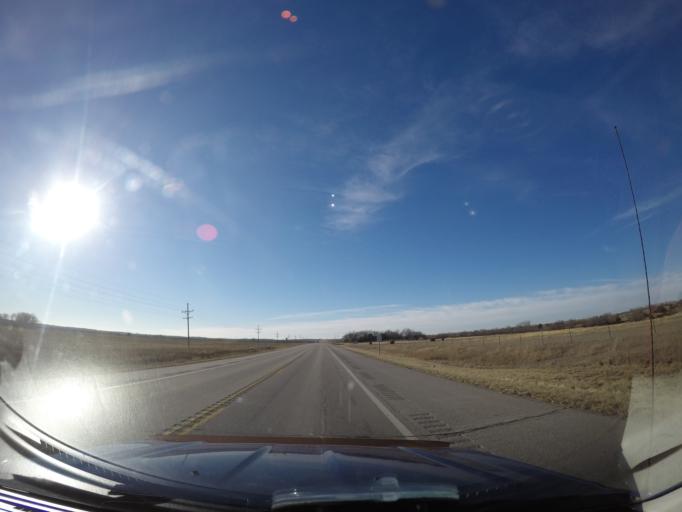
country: US
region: Kansas
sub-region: Marion County
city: Hillsboro
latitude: 38.3624
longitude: -97.3100
